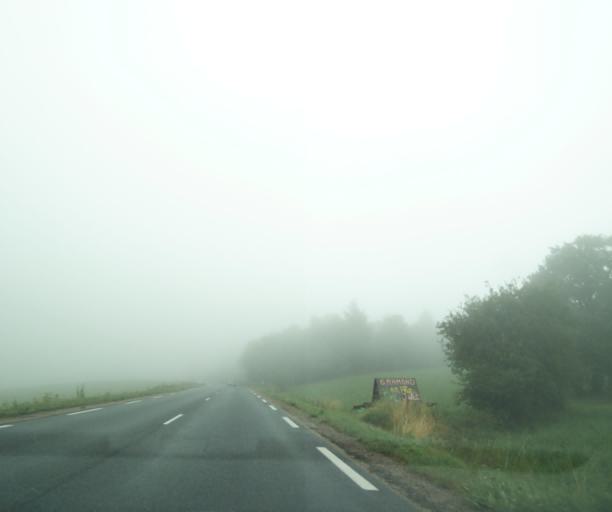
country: FR
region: Midi-Pyrenees
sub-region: Departement de l'Aveyron
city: Baraqueville
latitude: 44.2636
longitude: 2.4181
